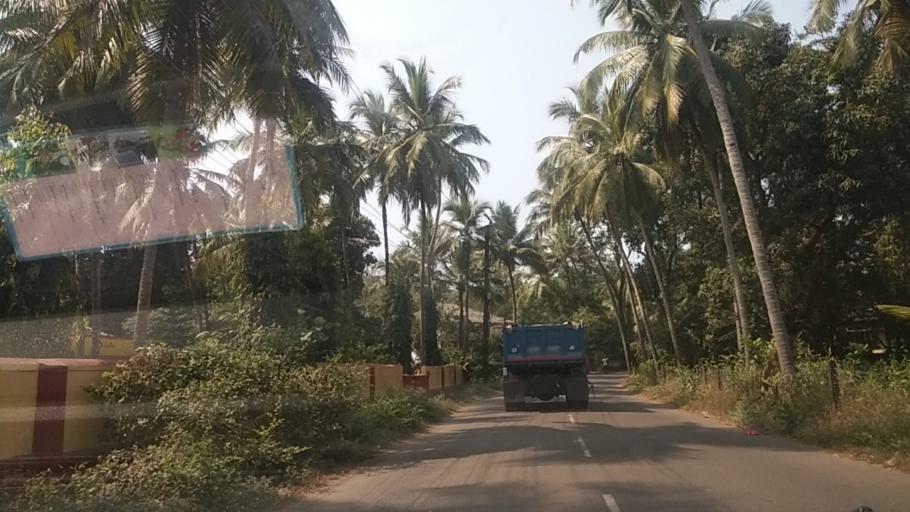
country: IN
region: Goa
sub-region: North Goa
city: Solim
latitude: 15.6120
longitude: 73.7741
